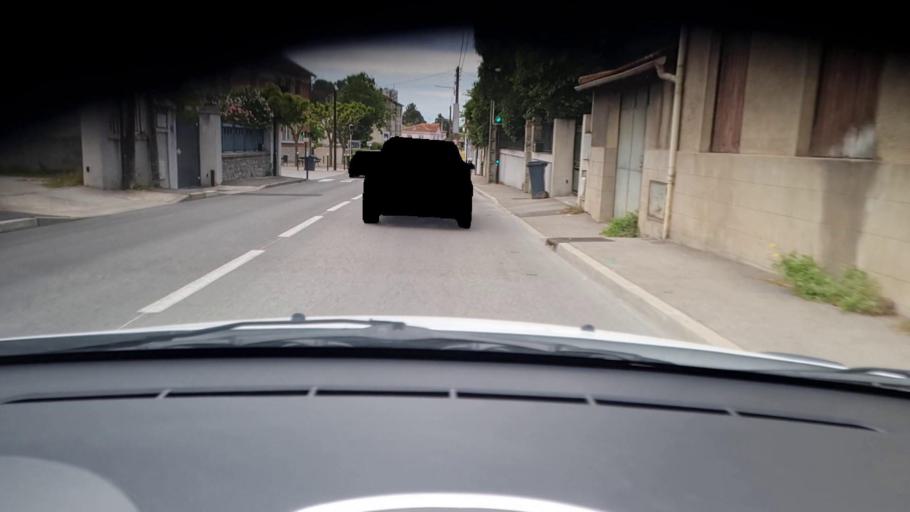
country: FR
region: Languedoc-Roussillon
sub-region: Departement du Gard
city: Nimes
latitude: 43.8540
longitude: 4.3795
